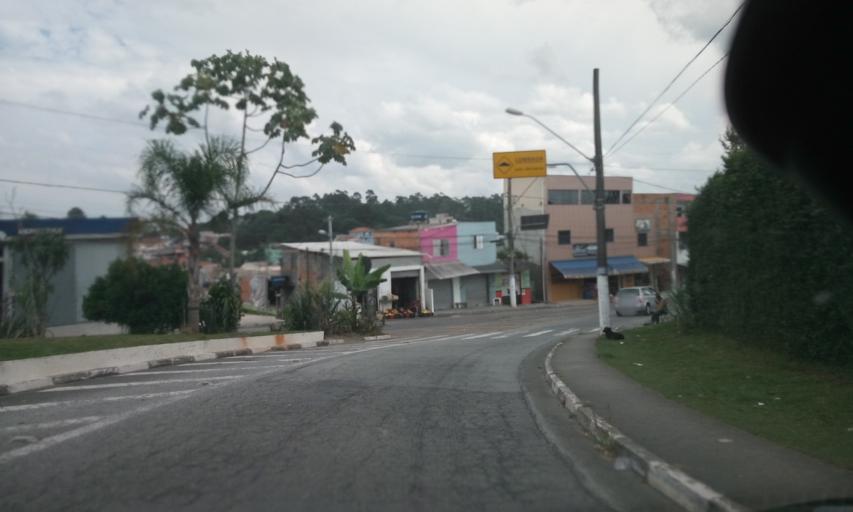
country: BR
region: Sao Paulo
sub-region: Sao Bernardo Do Campo
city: Sao Bernardo do Campo
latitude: -23.7716
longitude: -46.5982
